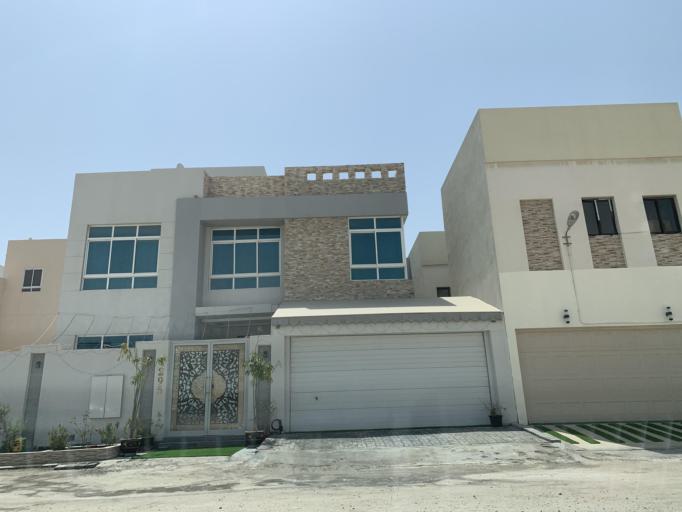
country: BH
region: Manama
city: Jidd Hafs
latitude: 26.1987
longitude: 50.5620
